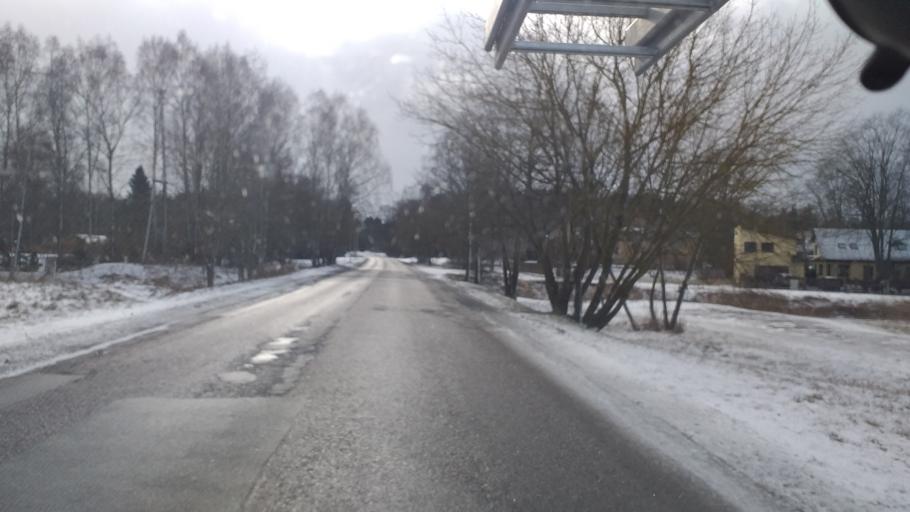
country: LV
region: Riga
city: Bolderaja
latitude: 56.9872
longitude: 24.0318
